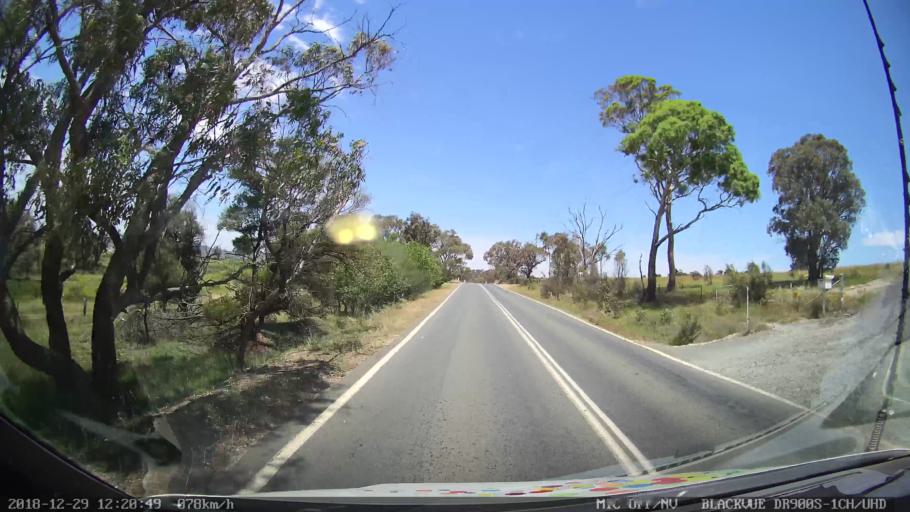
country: AU
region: New South Wales
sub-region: Queanbeyan
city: Queanbeyan
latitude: -35.4072
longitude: 149.2277
